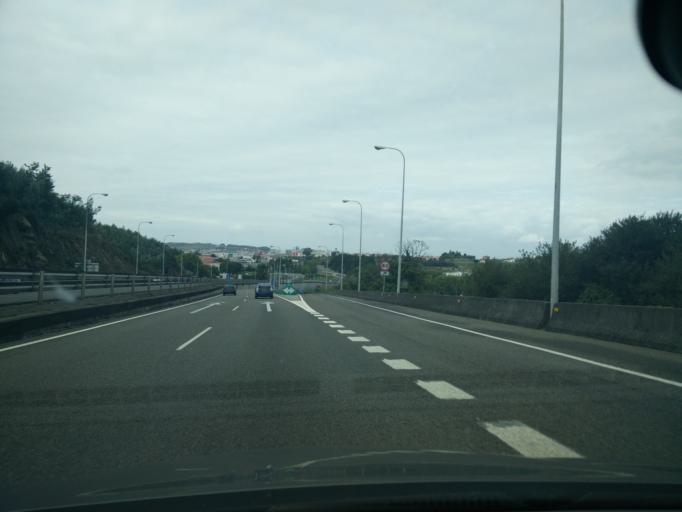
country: ES
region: Galicia
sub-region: Provincia da Coruna
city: Culleredo
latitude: 43.3260
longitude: -8.3944
